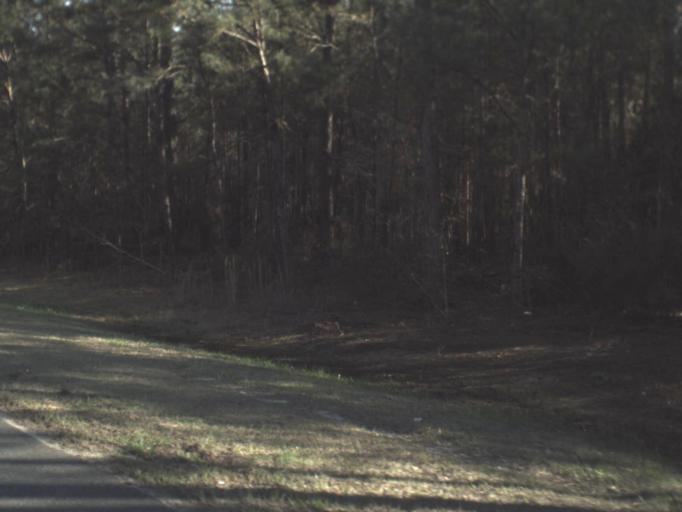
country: US
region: Florida
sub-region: Jackson County
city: Marianna
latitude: 30.7269
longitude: -85.0856
